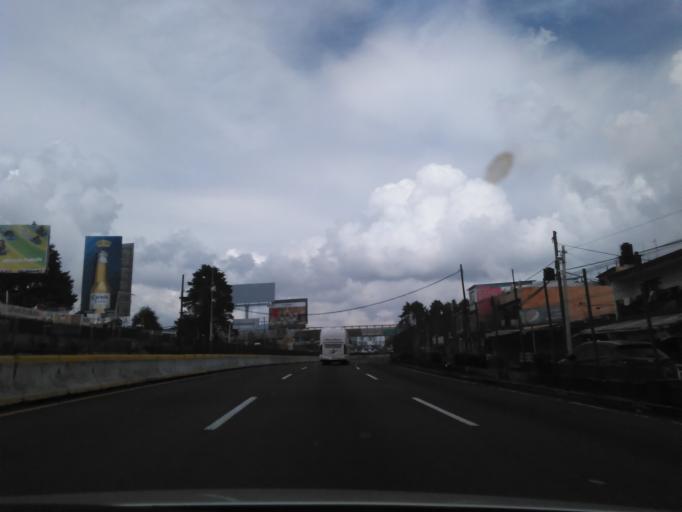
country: MX
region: Morelos
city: Tres Marias
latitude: 19.0541
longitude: -99.2417
